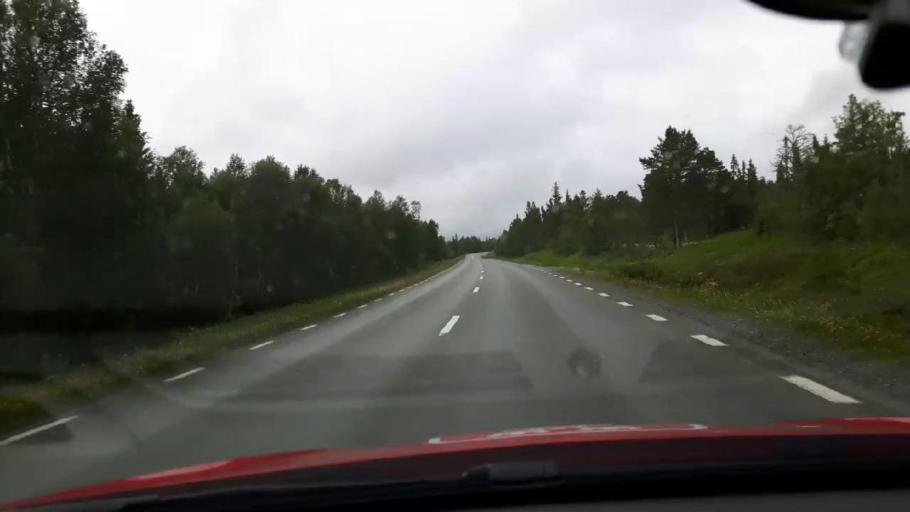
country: NO
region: Nord-Trondelag
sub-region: Meraker
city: Meraker
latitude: 63.2949
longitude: 12.1173
